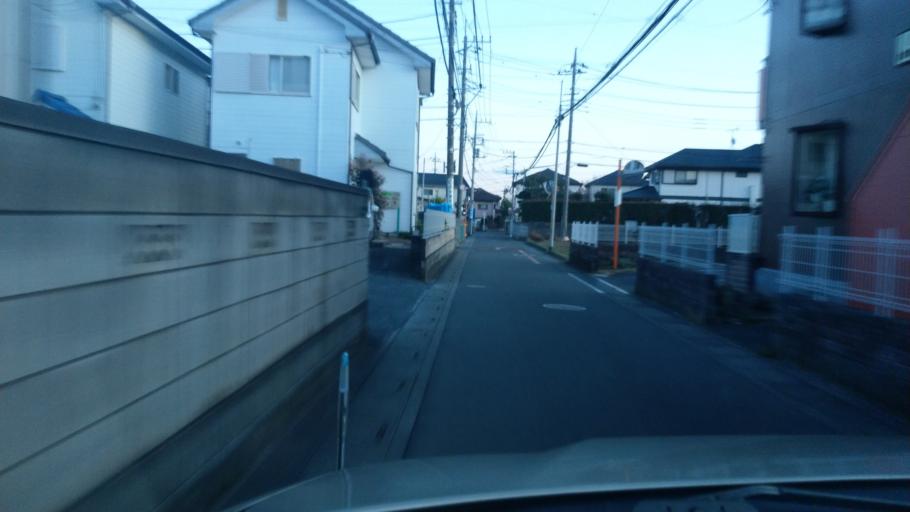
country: JP
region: Saitama
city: Yono
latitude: 35.9148
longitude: 139.5847
